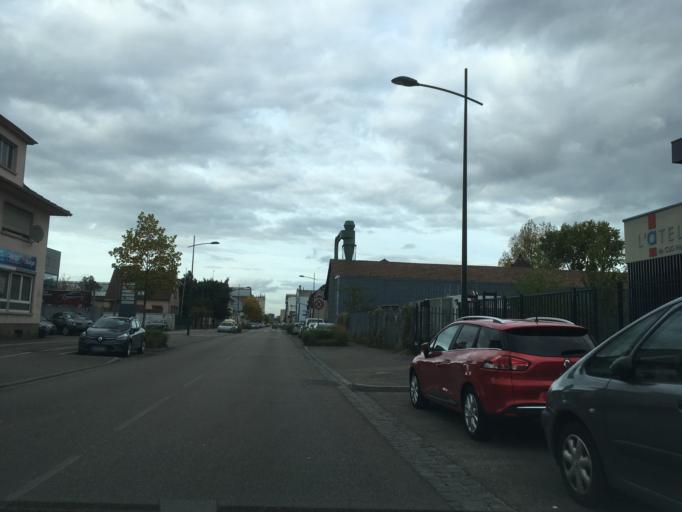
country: FR
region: Alsace
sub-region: Departement du Bas-Rhin
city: Strasbourg
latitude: 48.5561
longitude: 7.7377
